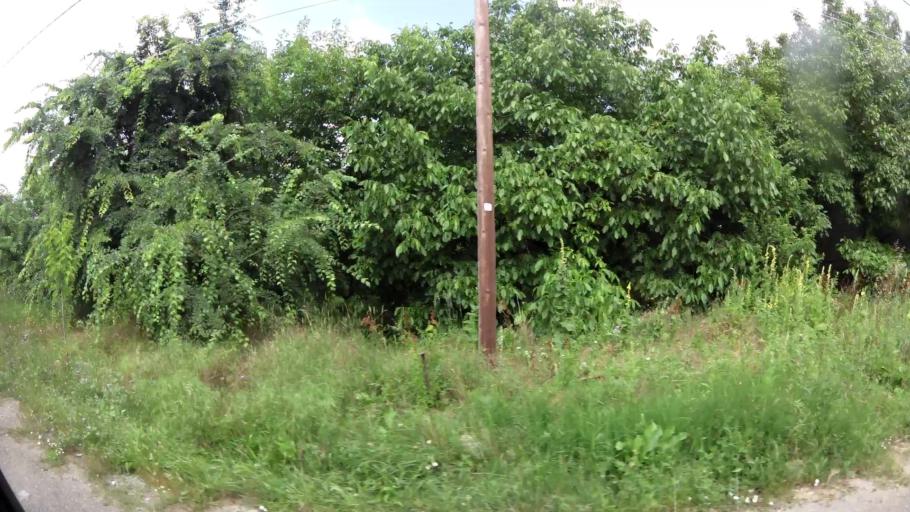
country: GR
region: West Macedonia
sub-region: Nomos Kozanis
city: Koila
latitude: 40.3523
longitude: 21.8345
